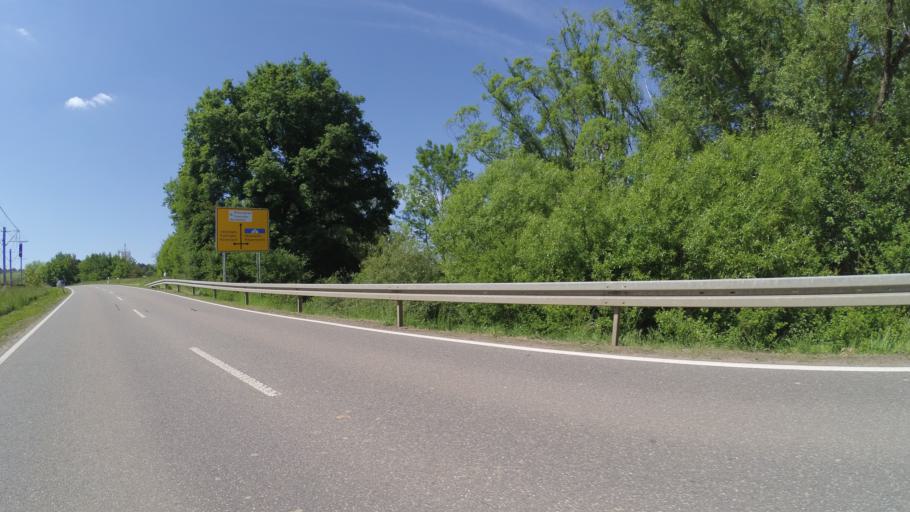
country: DE
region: Saarland
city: Riegelsberg
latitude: 49.3169
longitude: 6.9199
